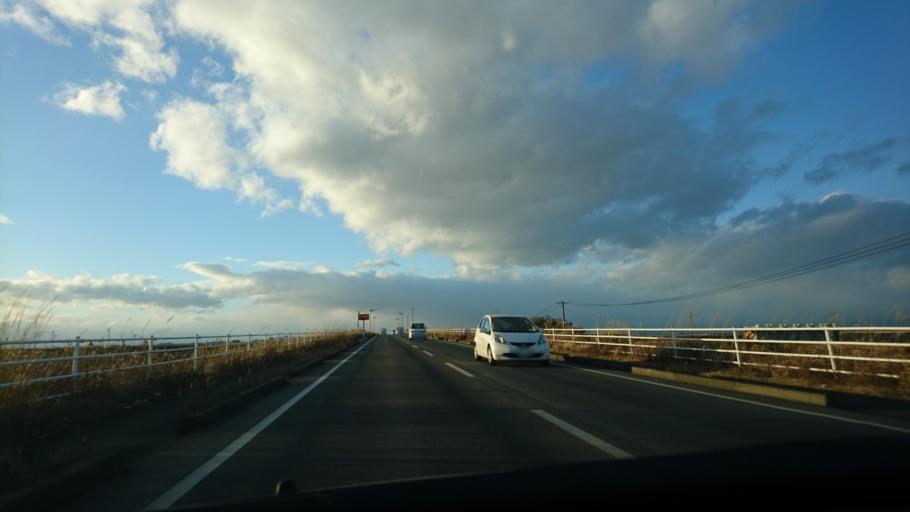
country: JP
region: Miyagi
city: Wakuya
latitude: 38.7200
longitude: 141.1571
